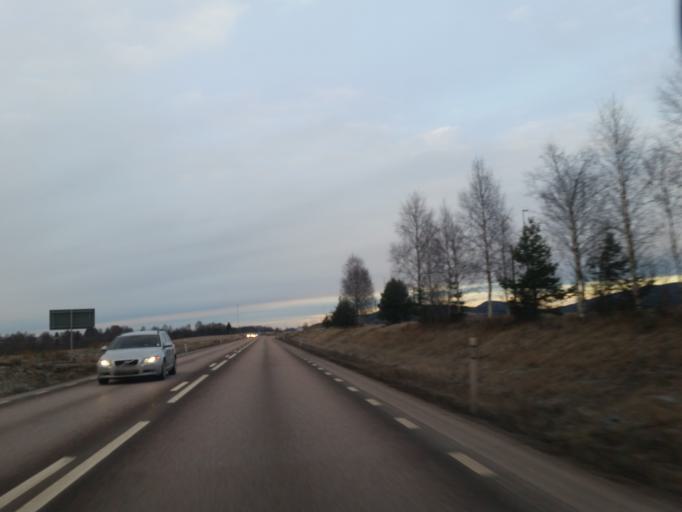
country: SE
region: Dalarna
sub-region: Leksand Municipality
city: Smedby
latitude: 60.6897
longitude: 15.0686
